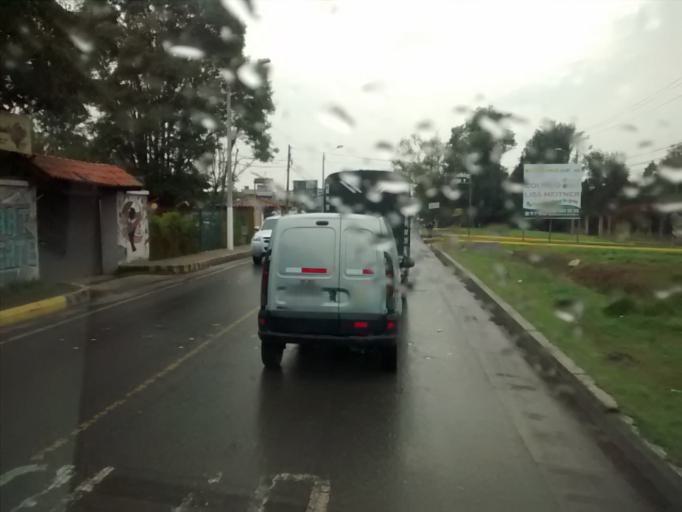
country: CO
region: Cundinamarca
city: Cota
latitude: 4.7631
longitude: -74.0904
